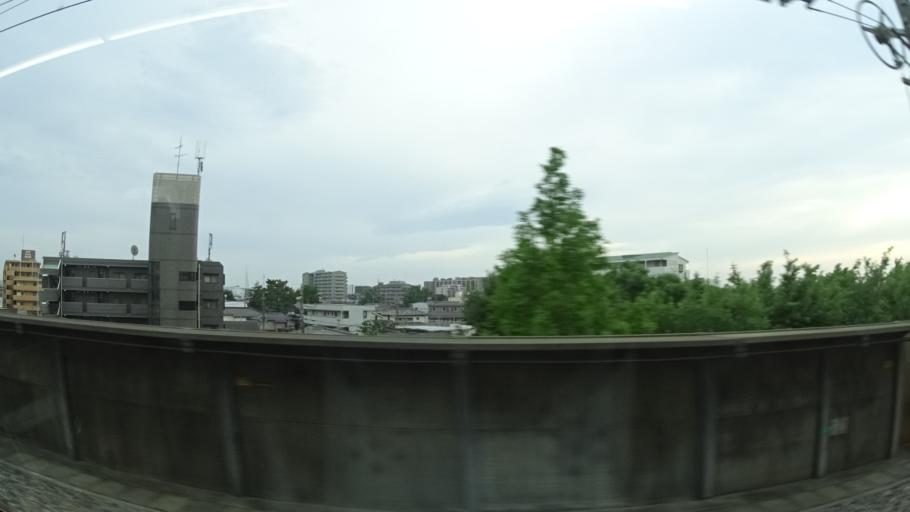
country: JP
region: Saitama
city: Shimotoda
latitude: 35.8104
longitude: 139.6751
